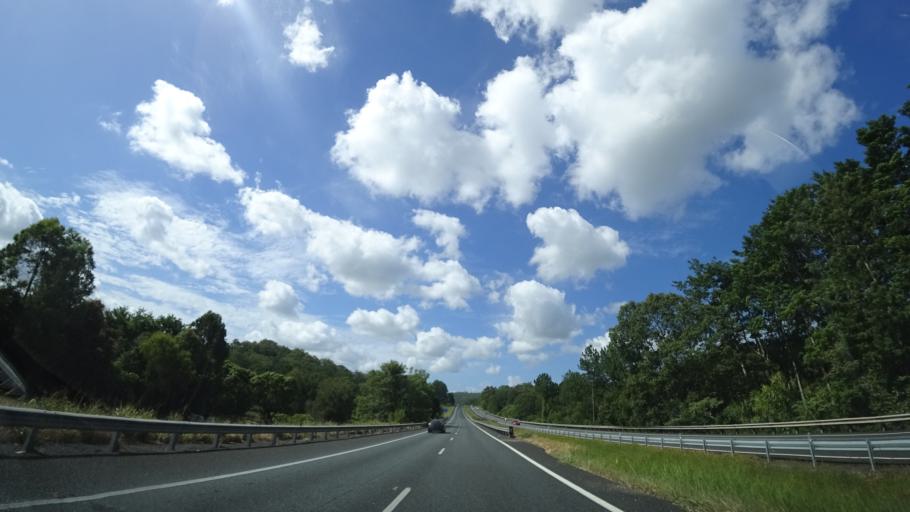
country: AU
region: Queensland
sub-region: Sunshine Coast
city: Twin Waters
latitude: -26.6322
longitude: 152.9878
